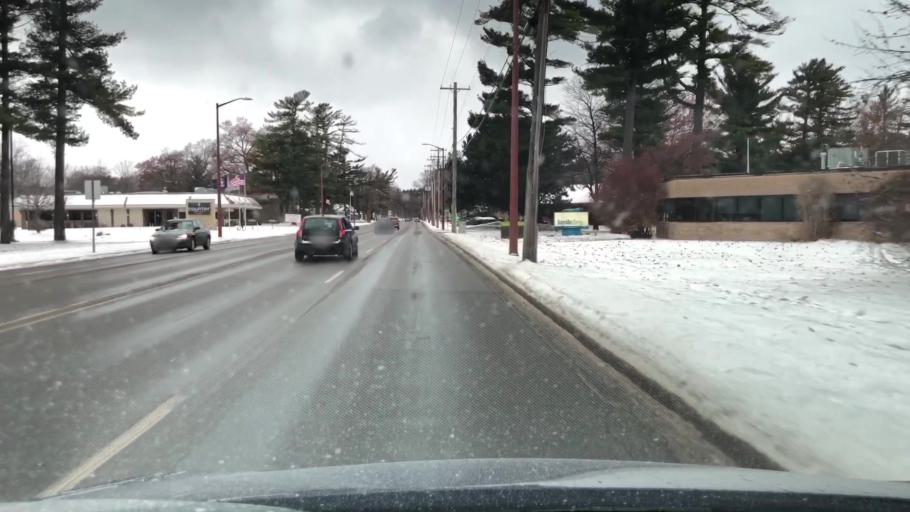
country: US
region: Michigan
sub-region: Grand Traverse County
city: Traverse City
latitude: 44.7598
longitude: -85.5808
